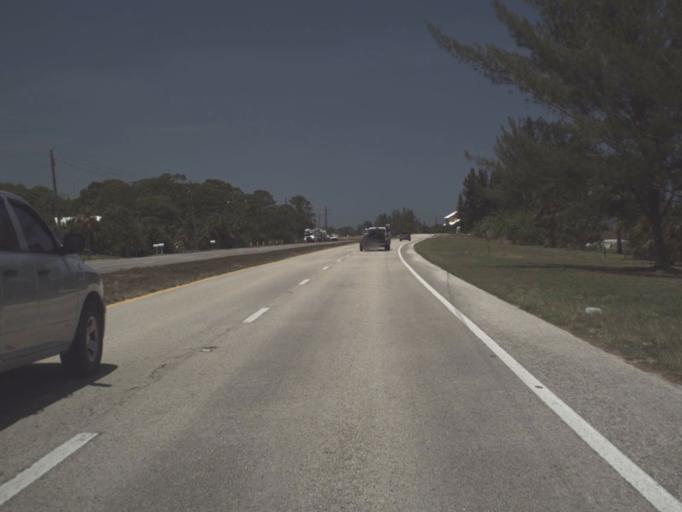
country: US
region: Florida
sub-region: Brevard County
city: Grant-Valkaria
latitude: 27.9518
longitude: -80.5363
